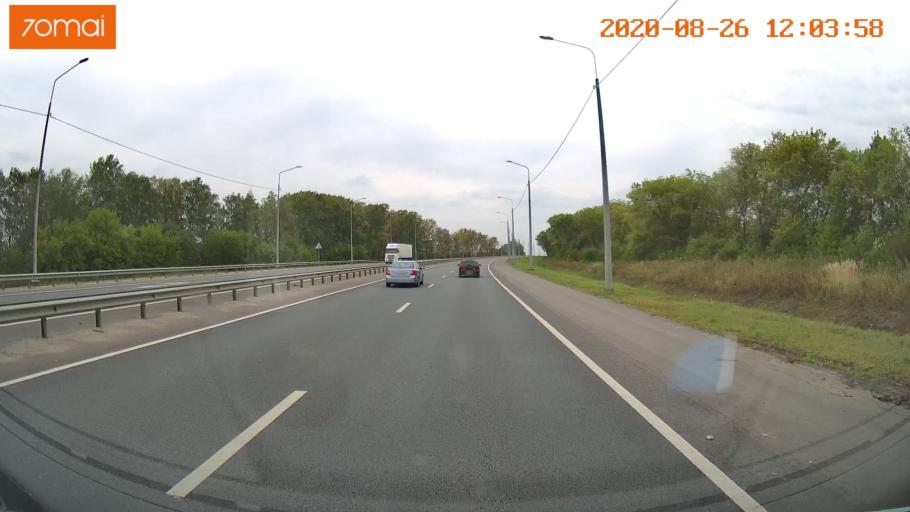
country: RU
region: Rjazan
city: Kiritsy
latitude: 54.3050
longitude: 40.1965
